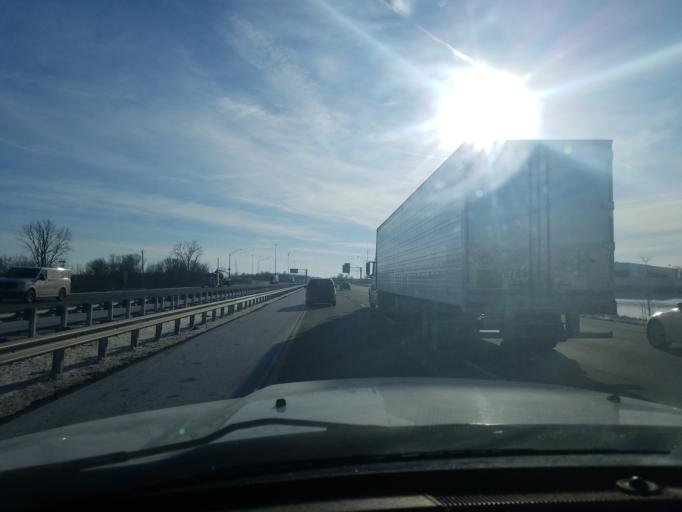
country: US
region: Indiana
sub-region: Madison County
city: Pendleton
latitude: 40.0110
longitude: -85.7694
